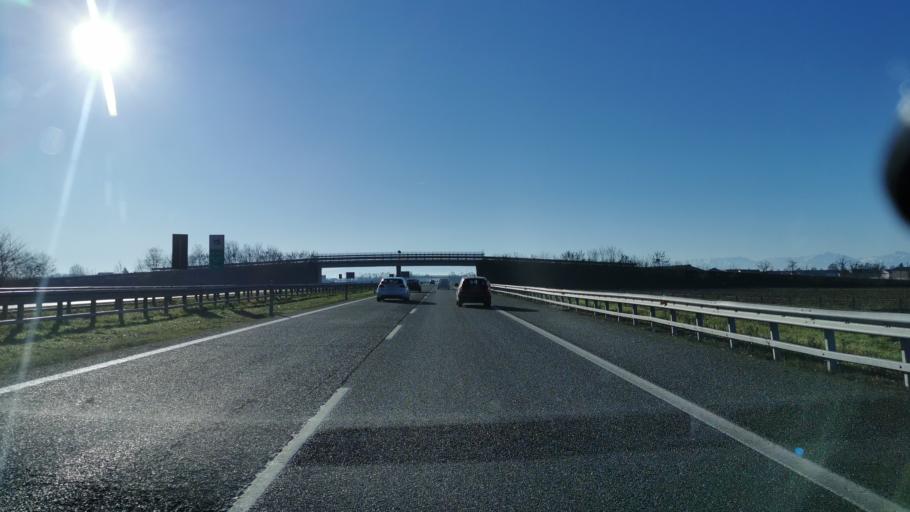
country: IT
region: Piedmont
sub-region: Provincia di Torino
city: Carmagnola
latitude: 44.8366
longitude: 7.7508
